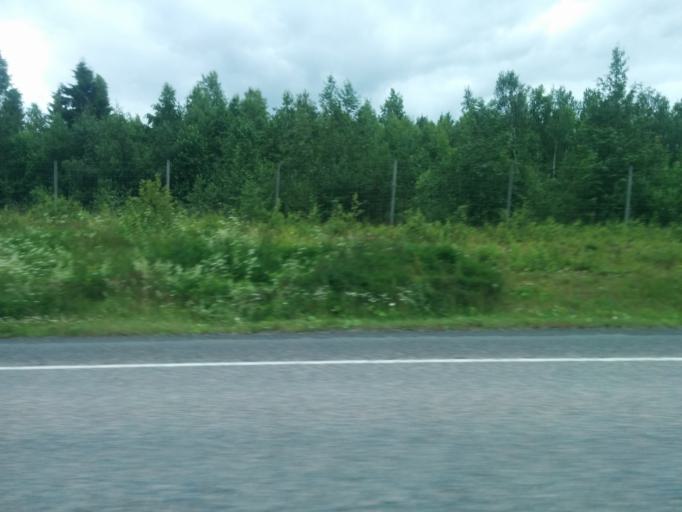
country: FI
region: Pirkanmaa
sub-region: Tampere
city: Orivesi
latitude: 61.7082
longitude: 24.4692
